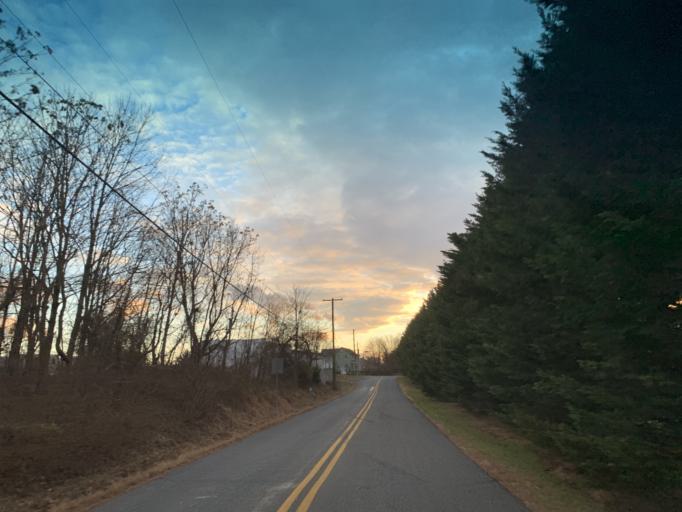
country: US
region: Maryland
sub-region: Harford County
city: South Bel Air
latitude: 39.5951
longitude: -76.3225
